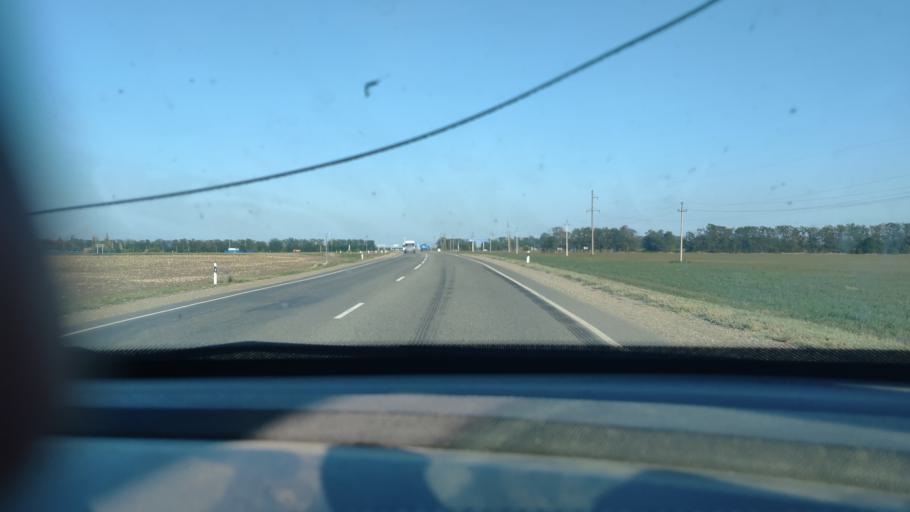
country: RU
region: Krasnodarskiy
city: Staroshcherbinovskaya
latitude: 46.6106
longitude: 38.6444
